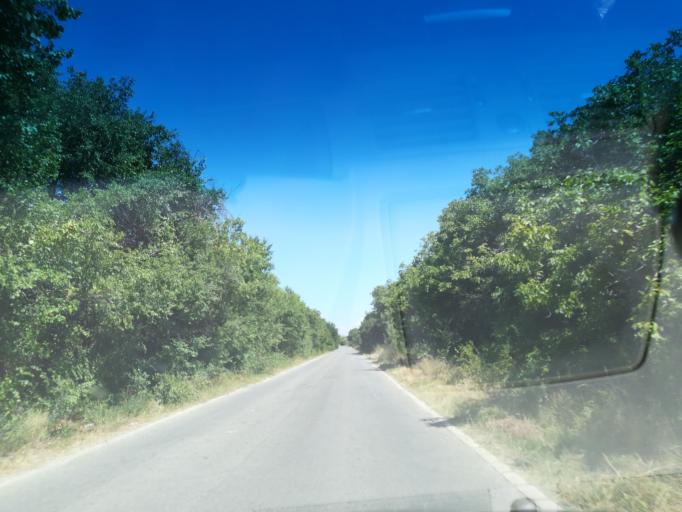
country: BG
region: Plovdiv
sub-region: Obshtina Sadovo
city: Sadovo
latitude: 42.0252
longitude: 24.9909
